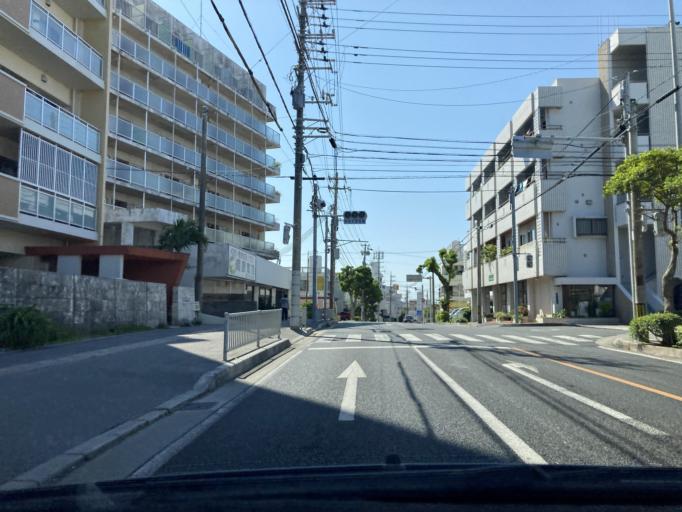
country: JP
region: Okinawa
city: Ginowan
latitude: 26.2488
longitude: 127.7263
